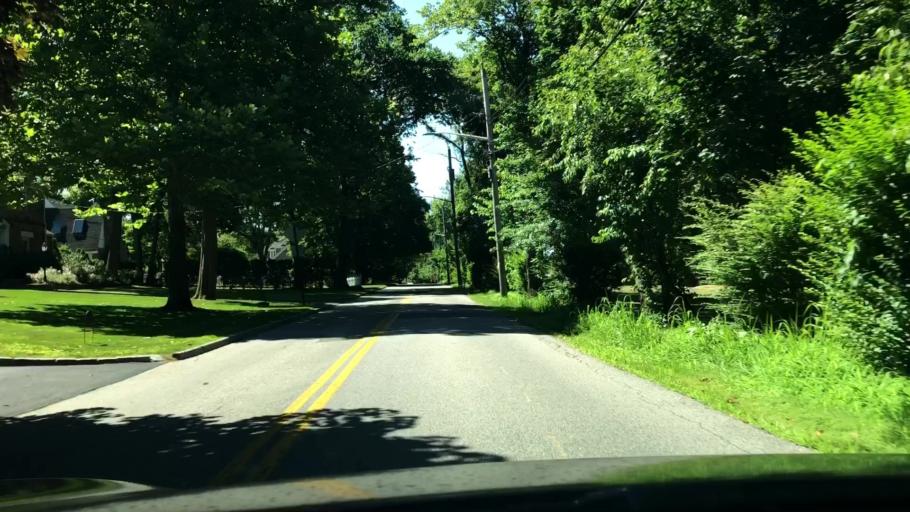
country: US
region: New York
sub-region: Westchester County
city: White Plains
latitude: 41.0200
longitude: -73.7474
